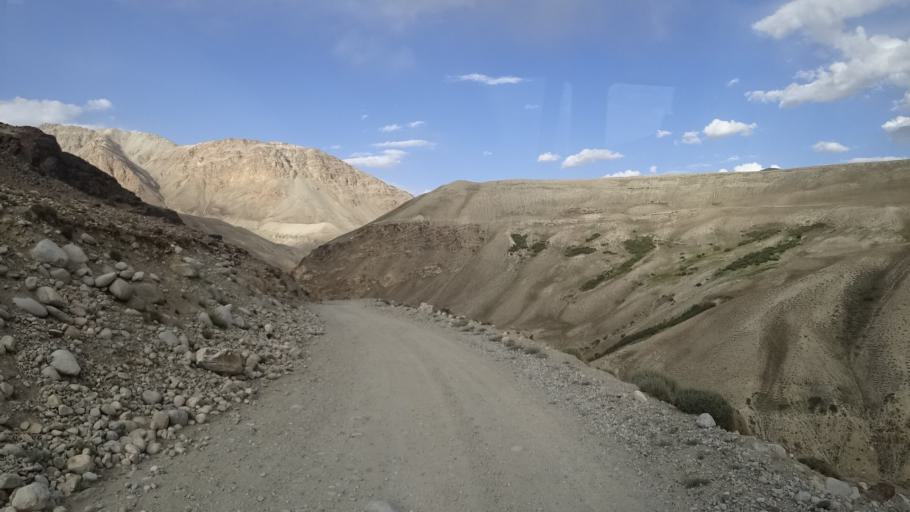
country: AF
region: Badakhshan
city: Khandud
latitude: 37.2268
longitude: 72.8063
